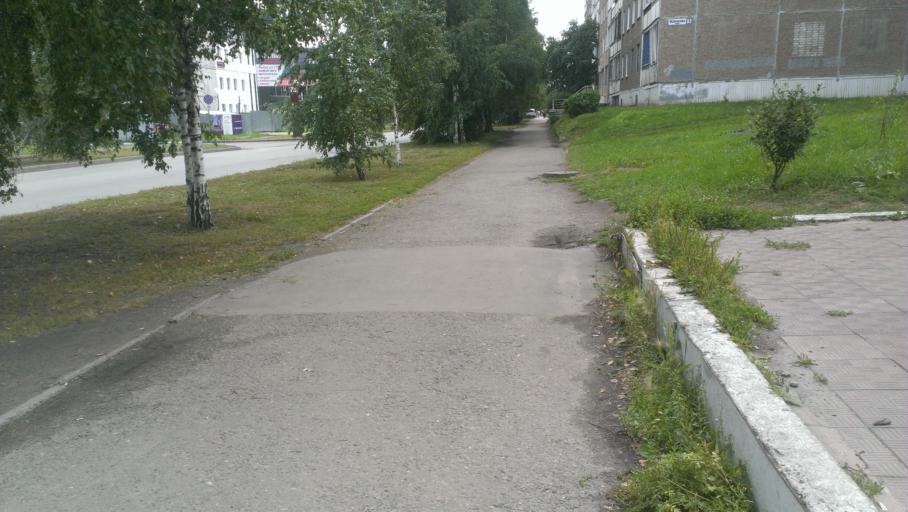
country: RU
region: Altai Krai
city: Novosilikatnyy
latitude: 53.3387
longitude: 83.6778
